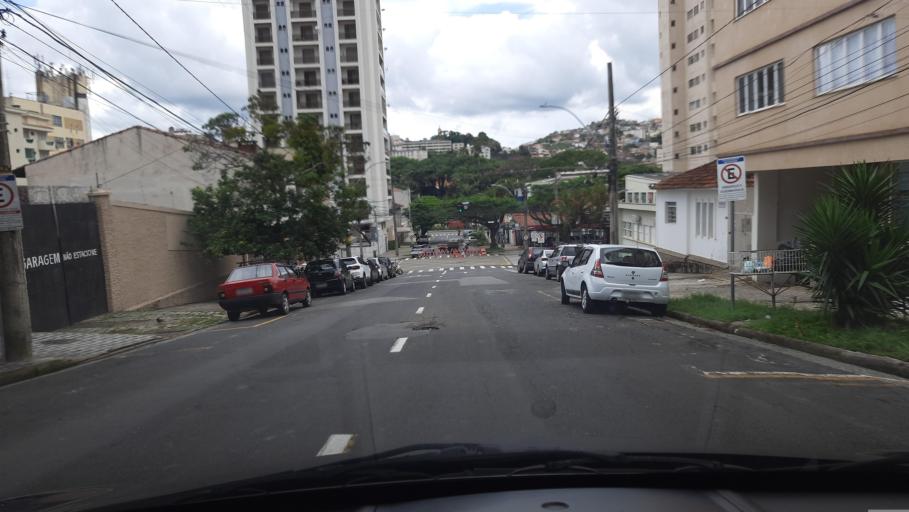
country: BR
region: Minas Gerais
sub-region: Pocos De Caldas
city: Pocos de Caldas
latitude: -21.7836
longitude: -46.5683
